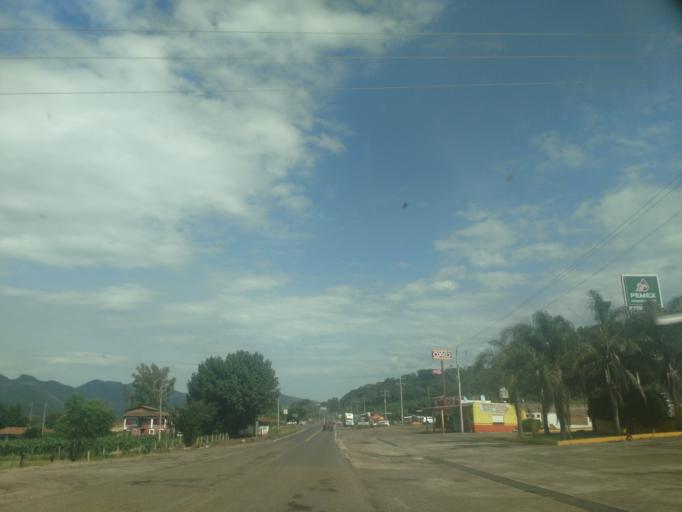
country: MX
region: Jalisco
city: Mascota
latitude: 20.4425
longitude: -104.7528
